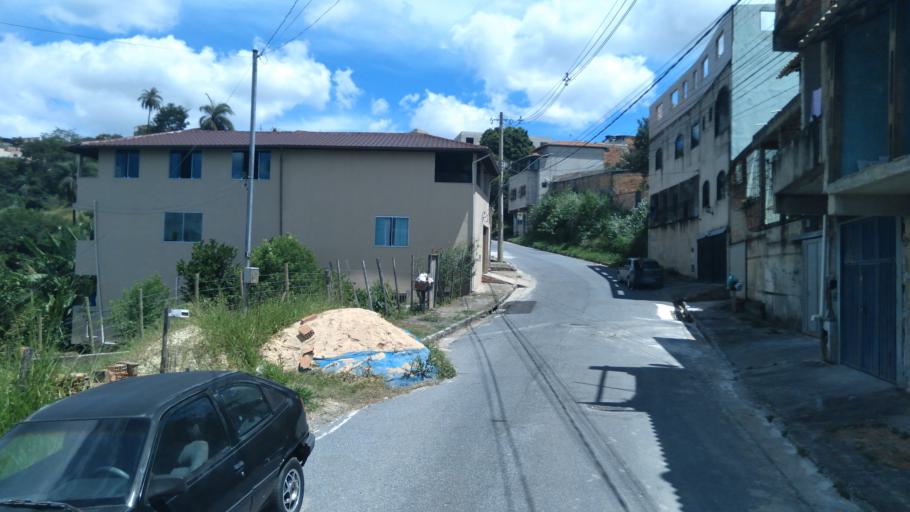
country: BR
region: Minas Gerais
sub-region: Santa Luzia
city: Santa Luzia
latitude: -19.8533
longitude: -43.8791
